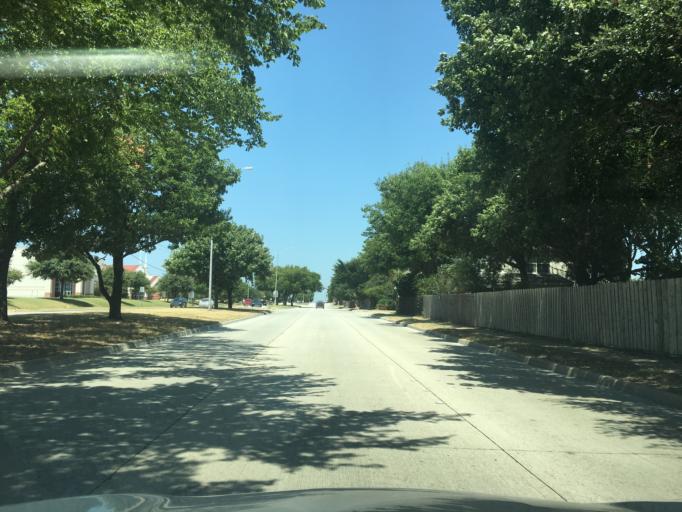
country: US
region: Texas
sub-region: Tarrant County
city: Edgecliff Village
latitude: 32.6281
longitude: -97.3698
